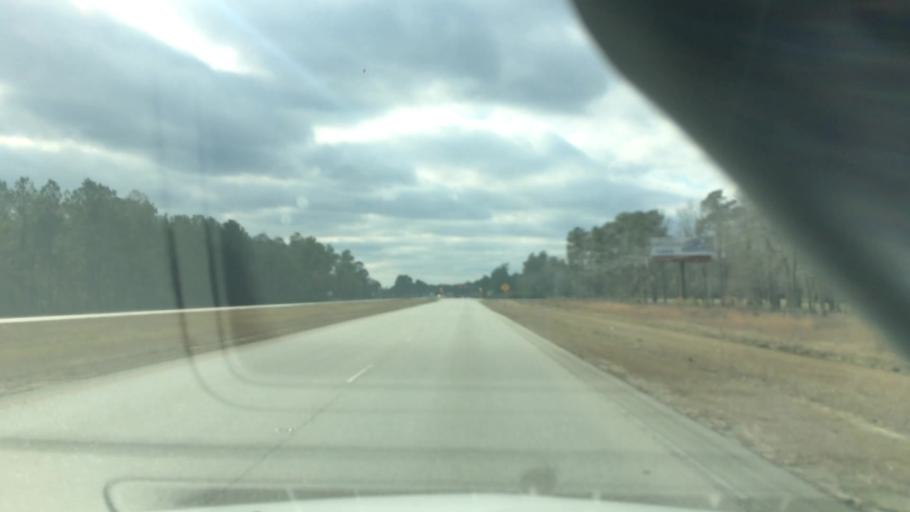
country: US
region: North Carolina
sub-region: Brunswick County
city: Bolivia
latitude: 34.0415
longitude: -78.2415
